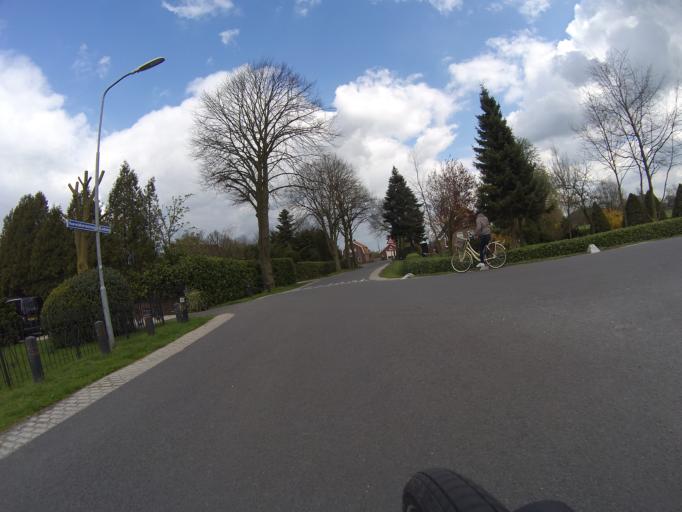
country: NL
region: Gelderland
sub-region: Gemeente Nijkerk
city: Nijkerk
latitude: 52.1904
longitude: 5.4557
